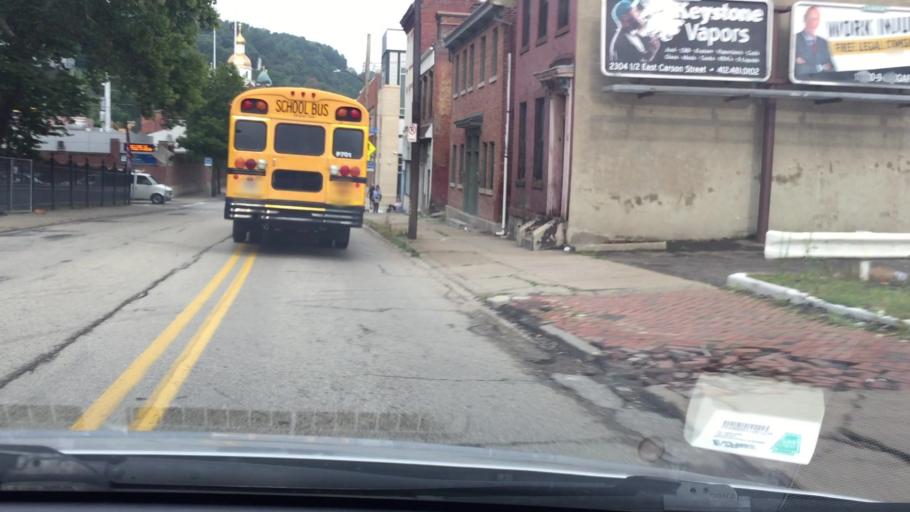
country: US
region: Pennsylvania
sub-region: Allegheny County
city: Pittsburgh
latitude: 40.4287
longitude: -79.9891
